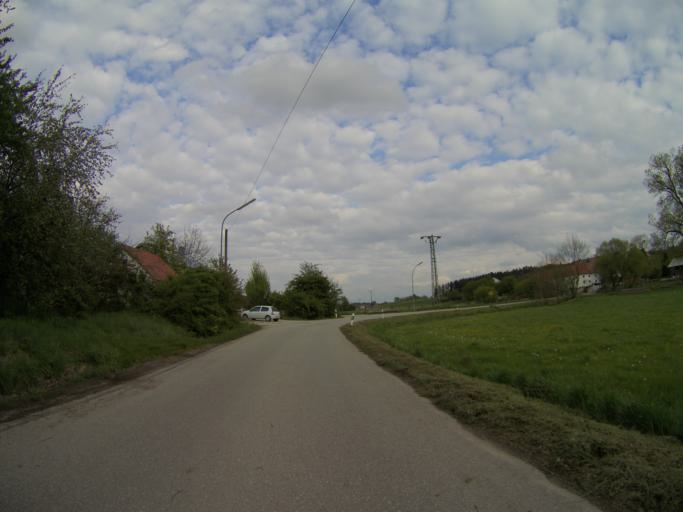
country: DE
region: Bavaria
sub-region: Upper Bavaria
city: Freising
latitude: 48.4262
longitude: 11.7558
